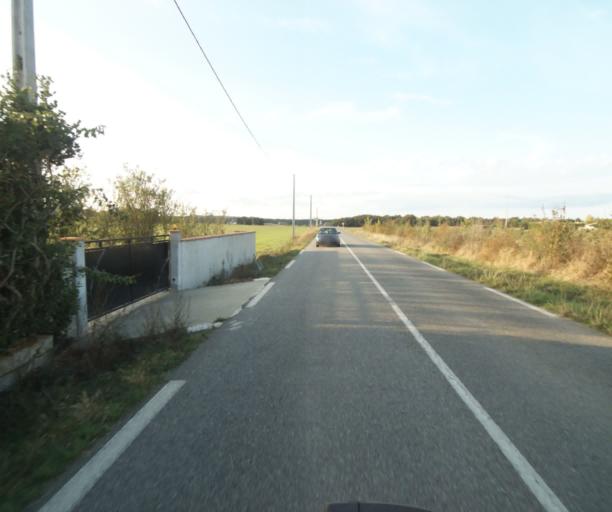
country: FR
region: Midi-Pyrenees
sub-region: Departement du Tarn-et-Garonne
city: Verdun-sur-Garonne
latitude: 43.8346
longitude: 1.1595
